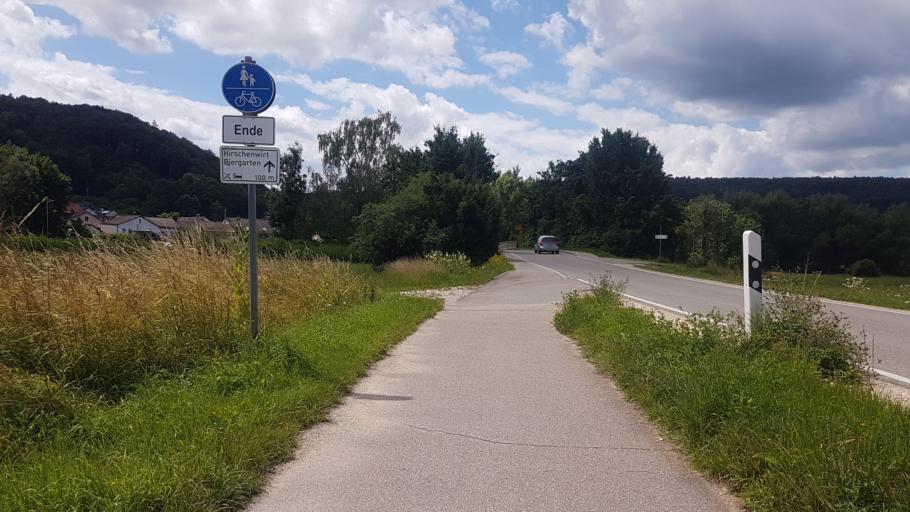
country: DE
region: Bavaria
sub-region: Upper Bavaria
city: Eichstaett
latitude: 48.8776
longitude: 11.1643
